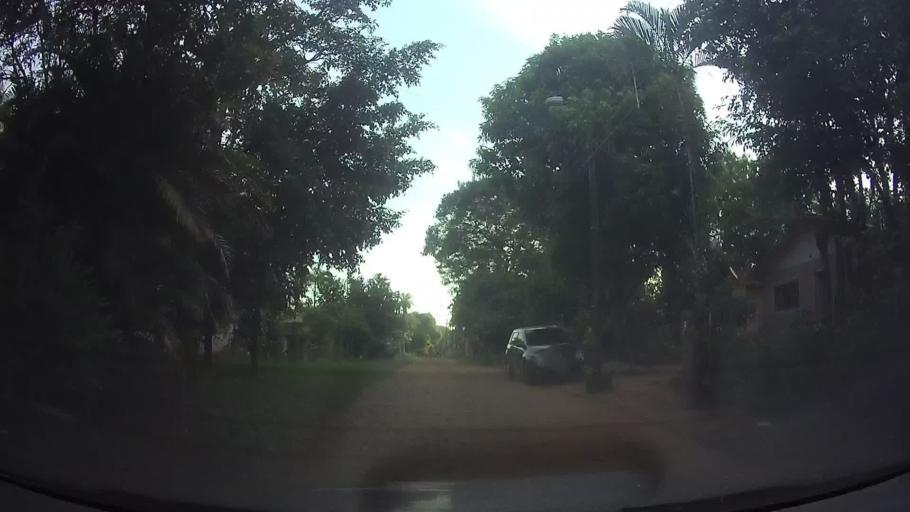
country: PY
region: Central
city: Limpio
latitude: -25.2395
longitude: -57.4465
